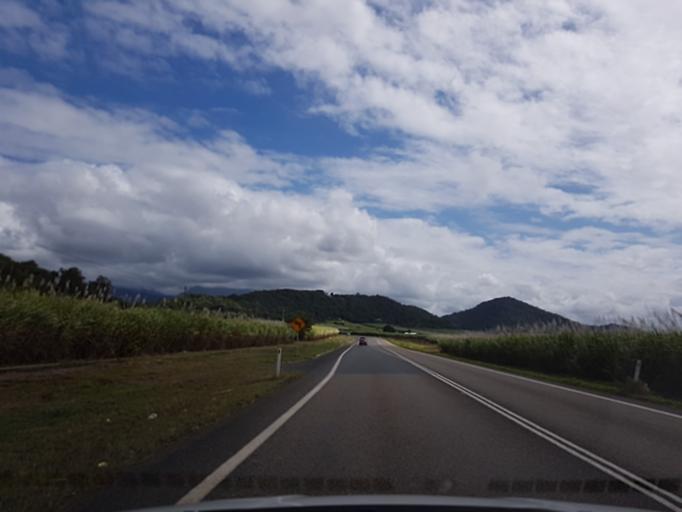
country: AU
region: Queensland
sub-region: Cairns
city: Port Douglas
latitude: -16.4803
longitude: 145.4070
